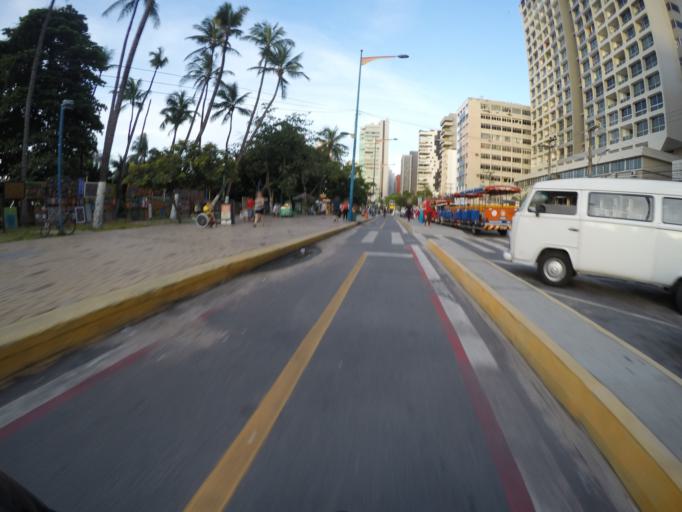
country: BR
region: Ceara
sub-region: Fortaleza
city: Fortaleza
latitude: -3.7257
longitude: -38.4928
